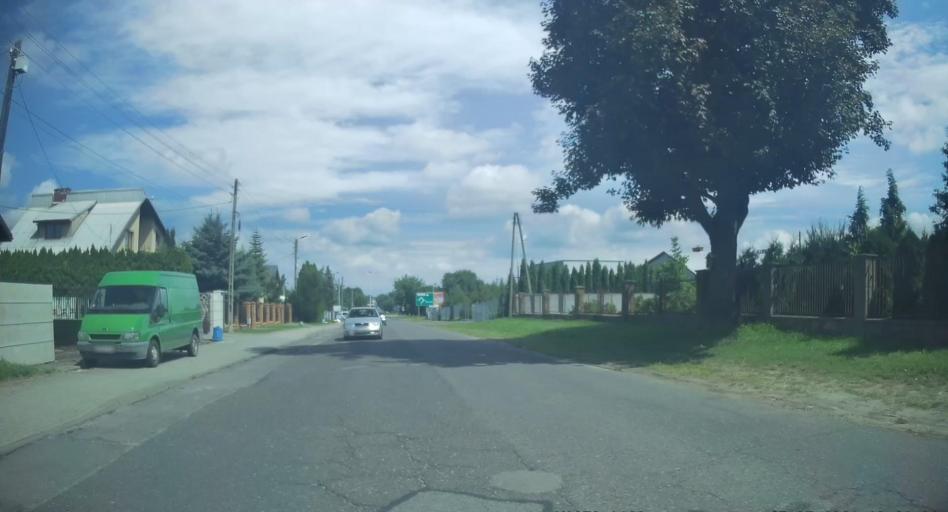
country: PL
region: Lodz Voivodeship
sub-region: Powiat rawski
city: Rawa Mazowiecka
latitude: 51.7505
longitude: 20.2403
